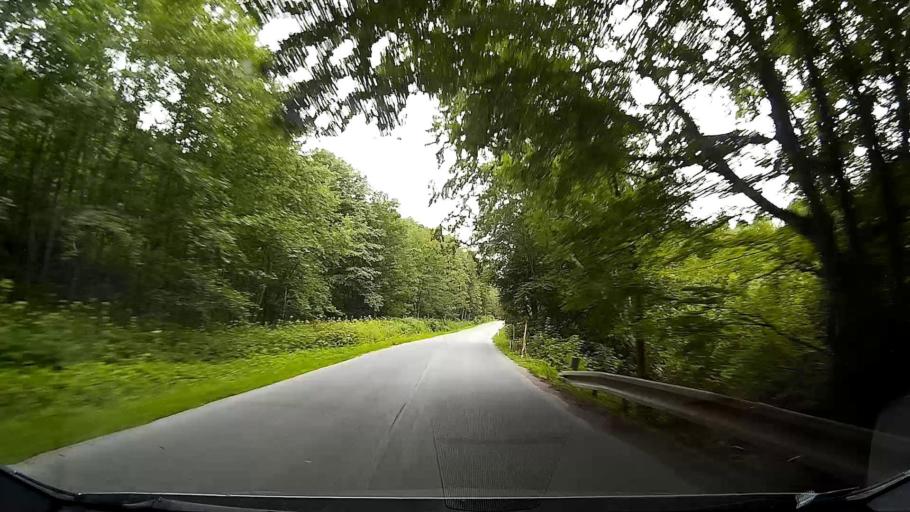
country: SK
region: Banskobystricky
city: Revuca
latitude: 48.7520
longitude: 20.0685
